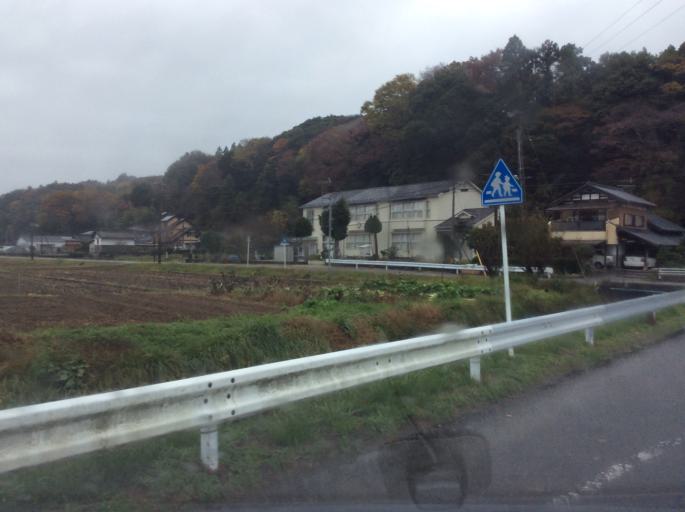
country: JP
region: Fukushima
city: Iwaki
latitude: 37.0909
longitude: 140.9407
